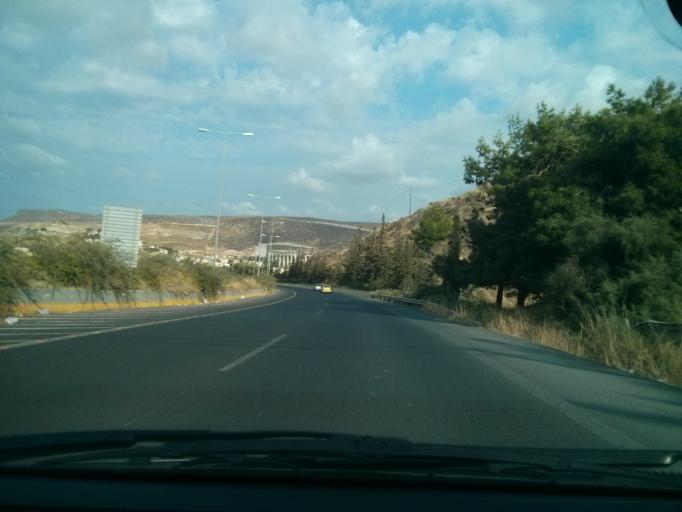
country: GR
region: Crete
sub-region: Nomos Irakleiou
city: Nea Alikarnassos
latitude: 35.3211
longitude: 25.1869
